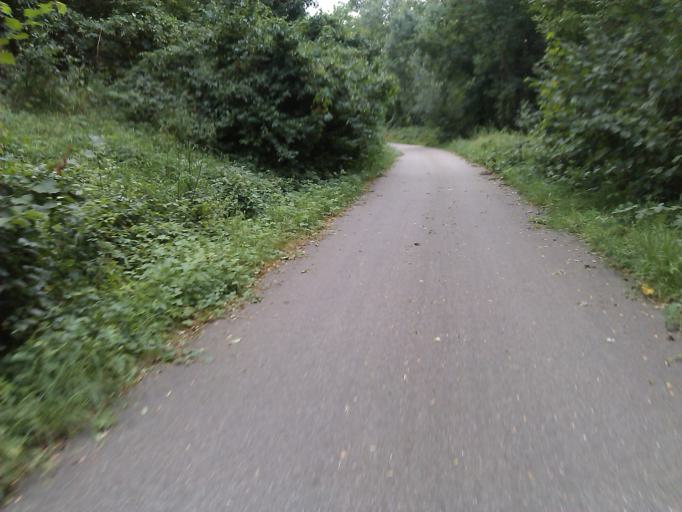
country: DE
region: Baden-Wuerttemberg
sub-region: Regierungsbezirk Stuttgart
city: Talheim
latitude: 49.1071
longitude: 9.1778
